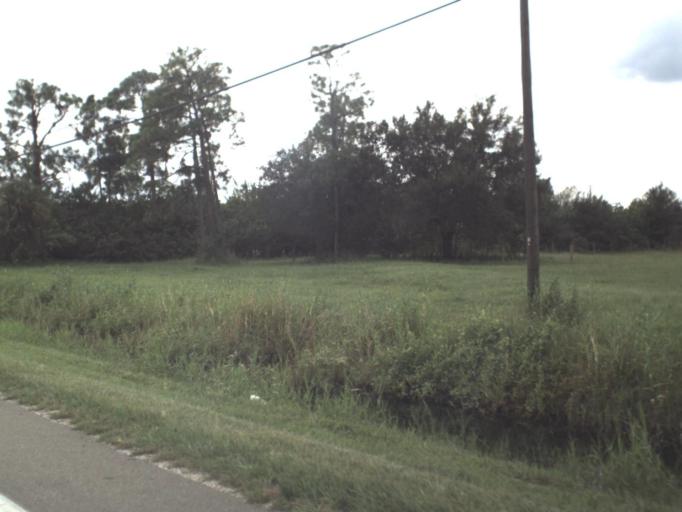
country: US
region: Florida
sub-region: Lee County
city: Fort Myers Shores
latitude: 26.7722
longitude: -81.7608
